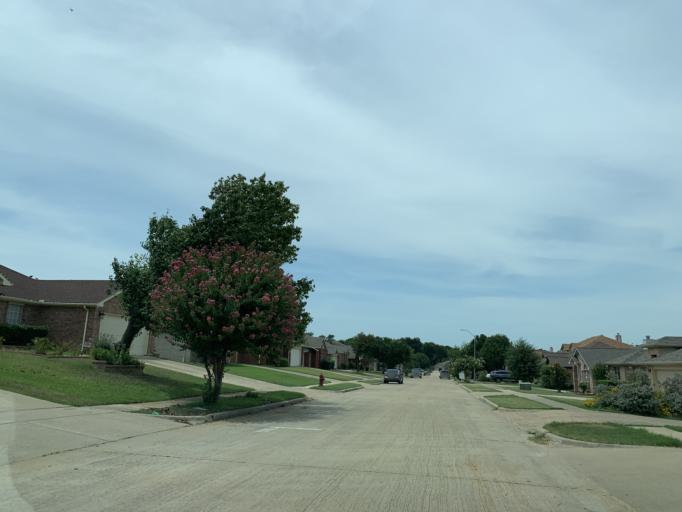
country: US
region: Texas
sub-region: Dallas County
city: Grand Prairie
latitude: 32.6653
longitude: -97.0202
